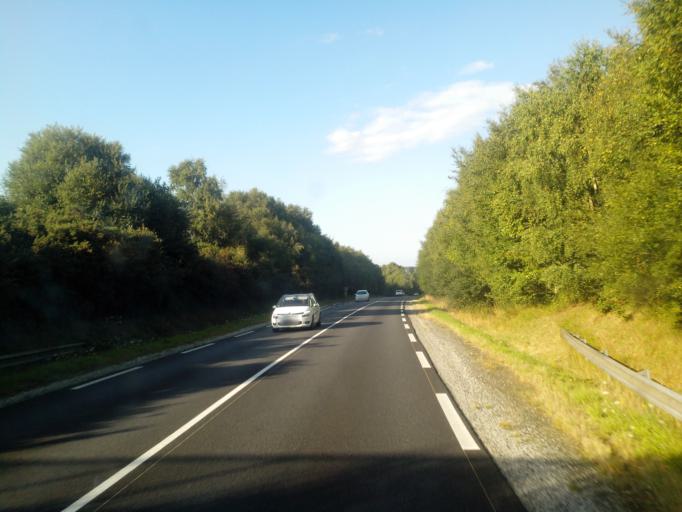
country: FR
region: Brittany
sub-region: Departement du Morbihan
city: Saint-Thuriau
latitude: 48.0164
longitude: -2.9710
